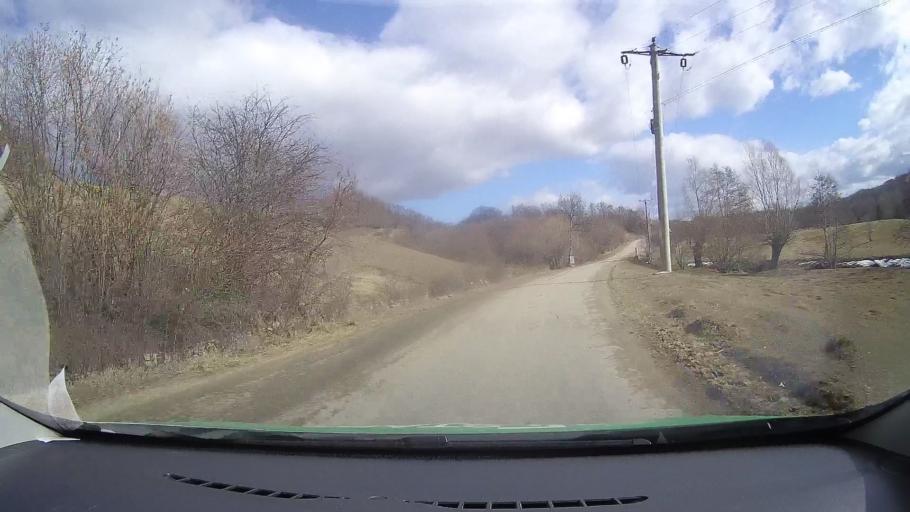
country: RO
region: Dambovita
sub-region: Comuna Motaeni
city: Motaeni
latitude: 45.1163
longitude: 25.4451
